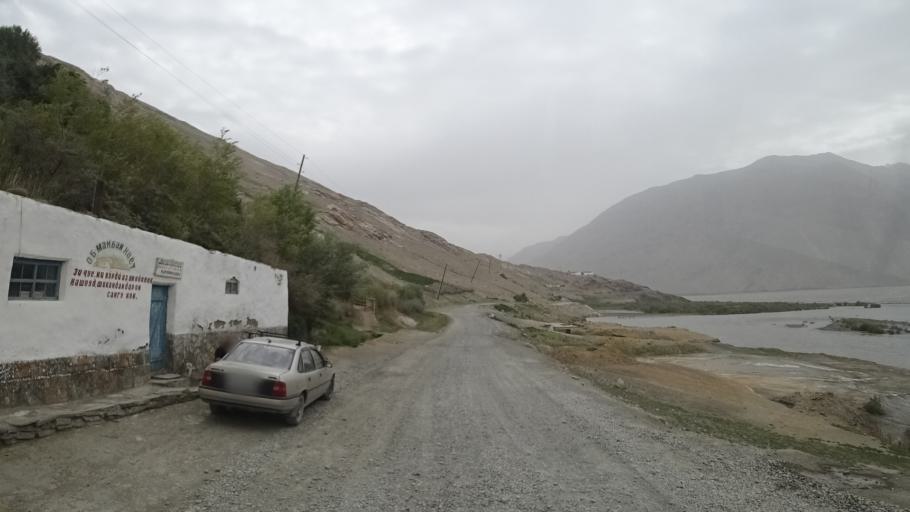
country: AF
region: Badakhshan
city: Khandud
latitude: 37.0052
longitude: 72.5376
